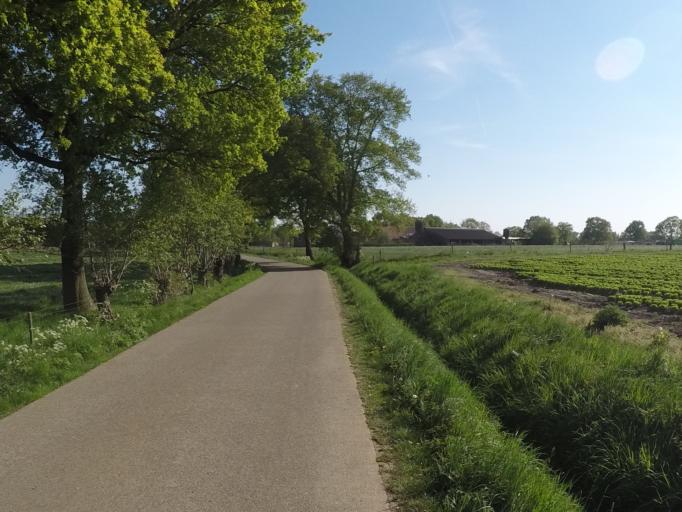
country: BE
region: Flanders
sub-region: Provincie Antwerpen
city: Nijlen
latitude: 51.1563
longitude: 4.7002
